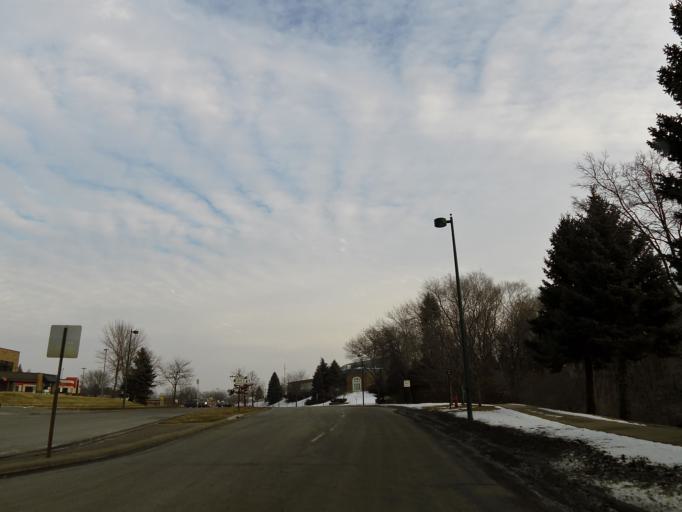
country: US
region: Minnesota
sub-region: Hennepin County
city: Eden Prairie
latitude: 44.8515
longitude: -93.4304
